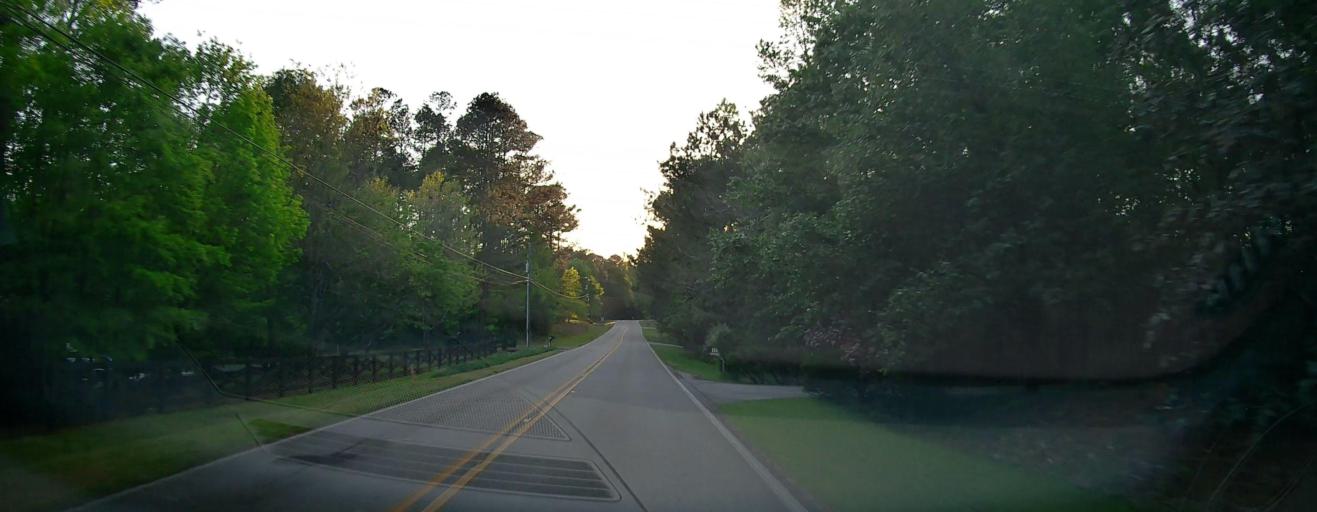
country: US
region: Georgia
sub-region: Henry County
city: Locust Grove
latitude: 33.4060
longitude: -84.1017
